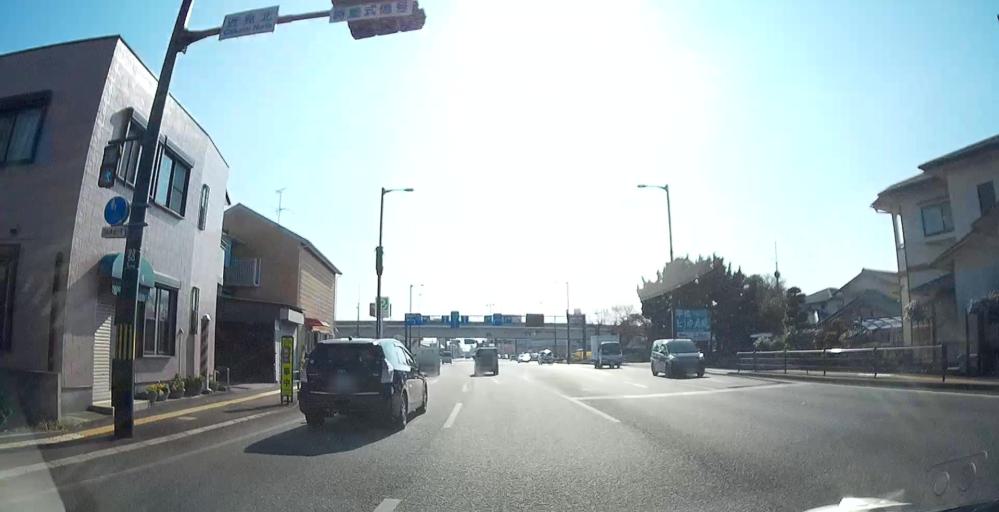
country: JP
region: Kumamoto
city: Kumamoto
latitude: 32.7636
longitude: 130.6900
